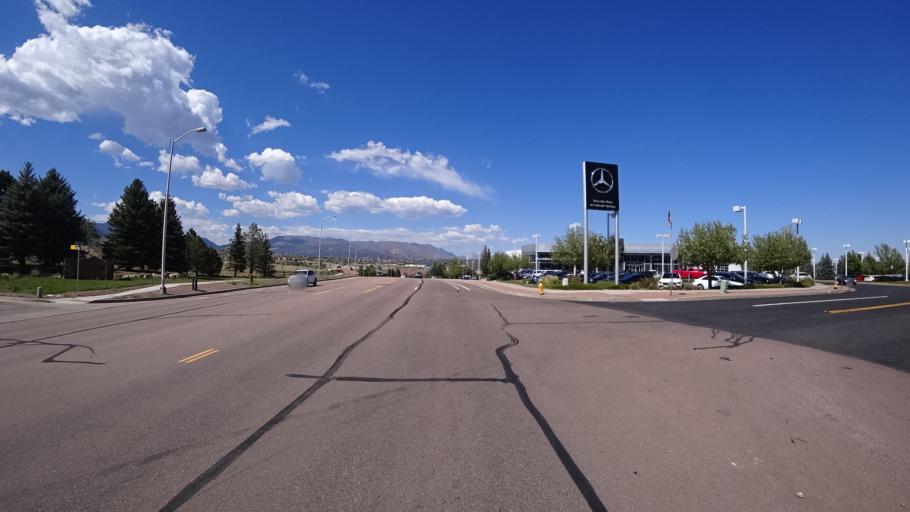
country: US
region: Colorado
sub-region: El Paso County
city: Colorado Springs
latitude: 38.8157
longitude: -104.8411
